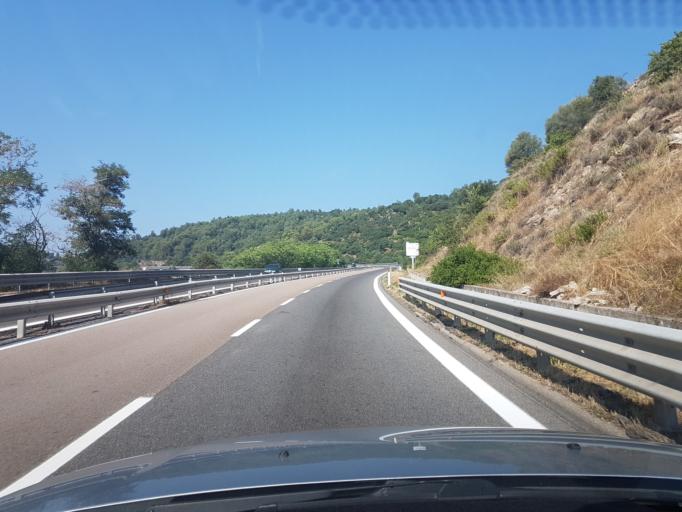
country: IT
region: Sardinia
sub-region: Provincia di Nuoro
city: Nuoro
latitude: 40.3399
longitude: 9.3082
